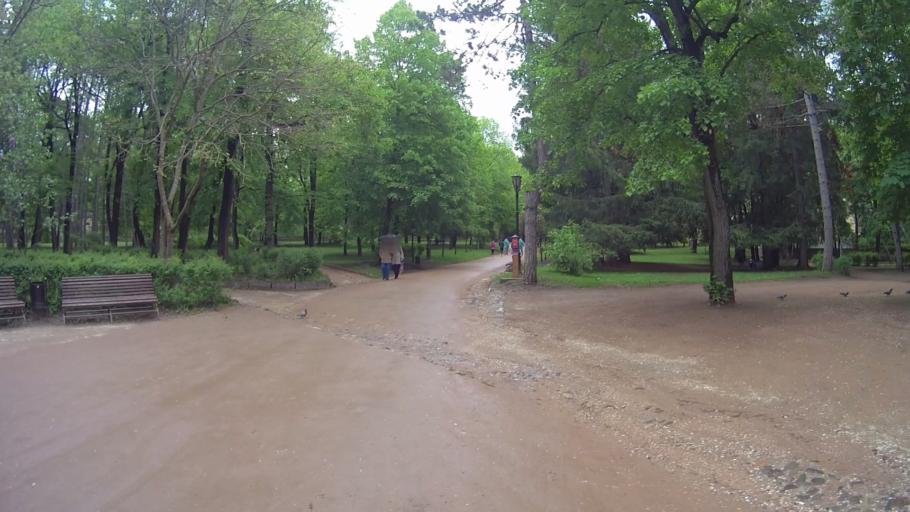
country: RU
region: Stavropol'skiy
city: Kislovodsk
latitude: 43.8953
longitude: 42.7195
